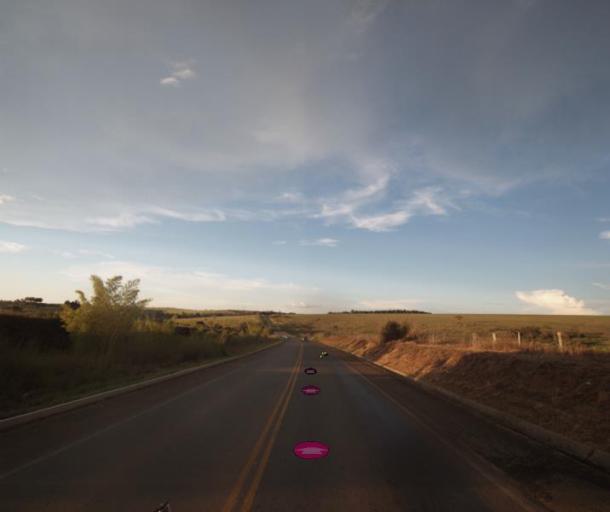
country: BR
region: Goias
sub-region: Anapolis
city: Anapolis
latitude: -16.1821
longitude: -48.9024
